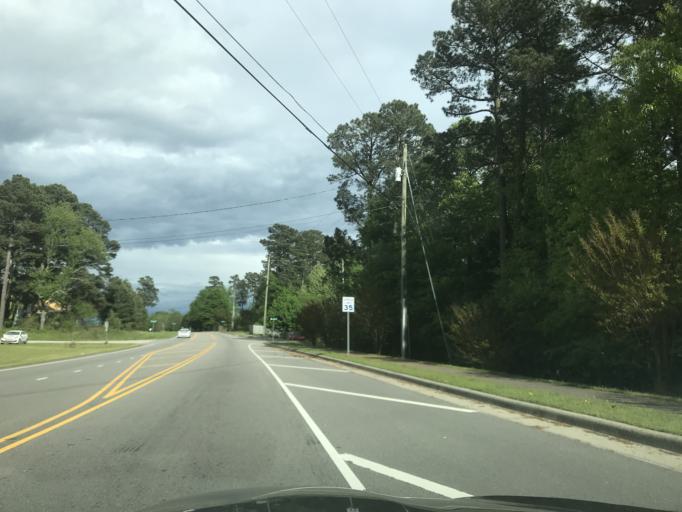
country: US
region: North Carolina
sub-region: Wake County
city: Raleigh
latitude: 35.8105
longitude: -78.5760
